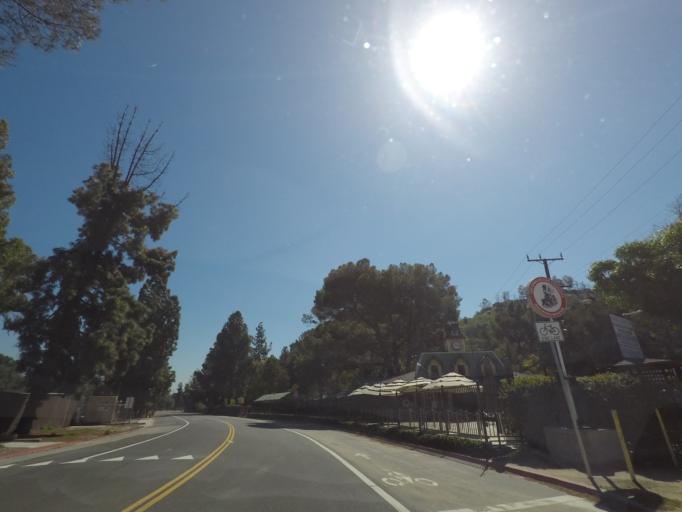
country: US
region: California
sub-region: Los Angeles County
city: Burbank
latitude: 34.1554
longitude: -118.3033
